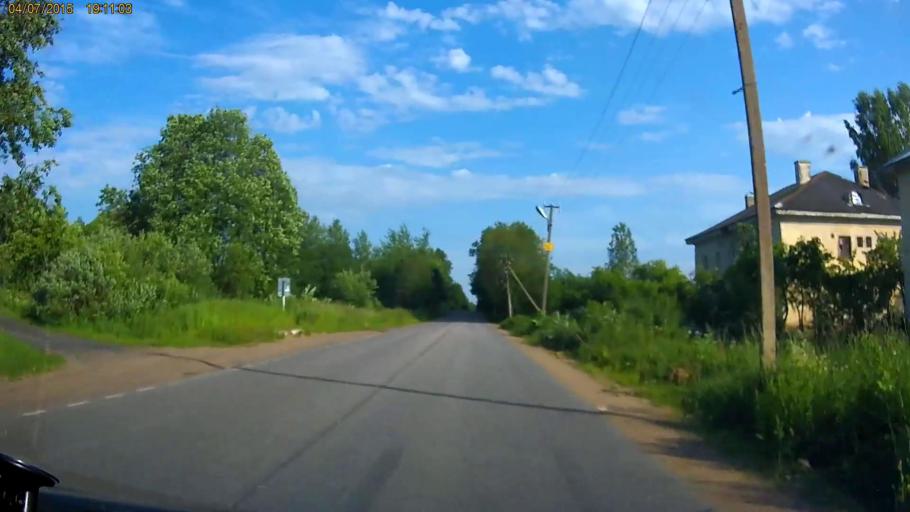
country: RU
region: Leningrad
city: Garbolovo
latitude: 60.3319
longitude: 30.4884
